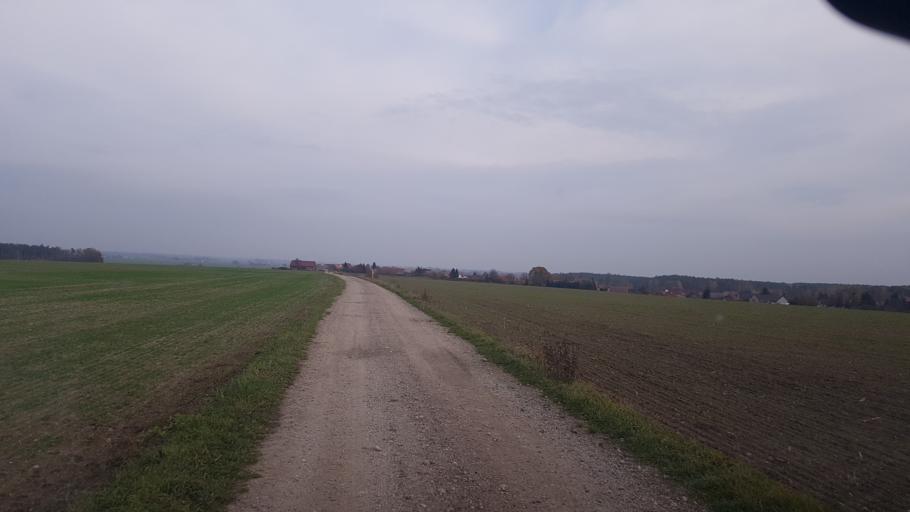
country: DE
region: Brandenburg
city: Schonborn
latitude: 51.6698
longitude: 13.4638
